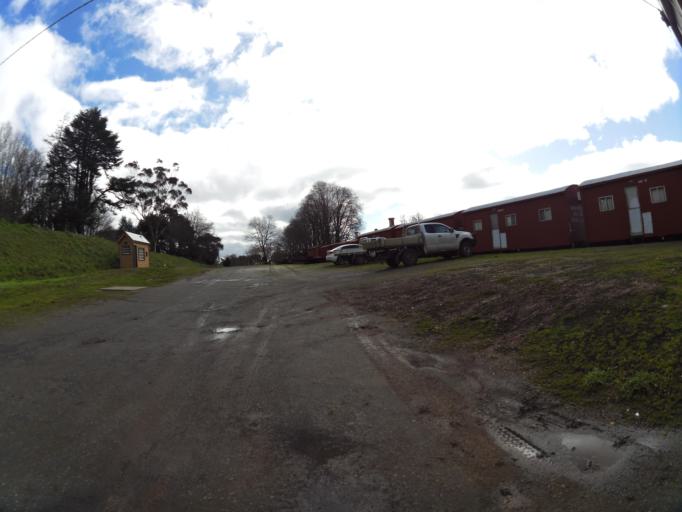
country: AU
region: Victoria
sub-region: Mount Alexander
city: Castlemaine
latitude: -37.3421
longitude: 144.1538
